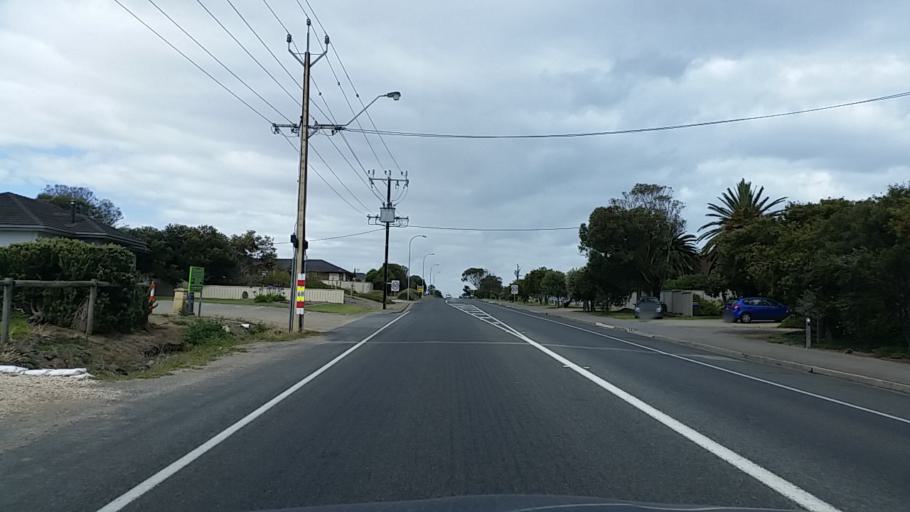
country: AU
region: South Australia
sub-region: Alexandrina
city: Port Elliot
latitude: -35.5317
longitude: 138.6711
